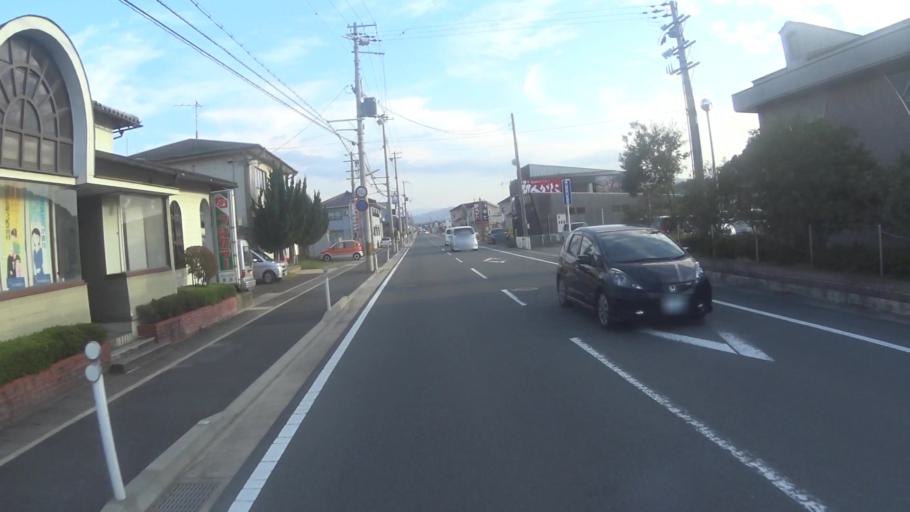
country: JP
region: Kyoto
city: Miyazu
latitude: 35.6258
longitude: 135.0727
